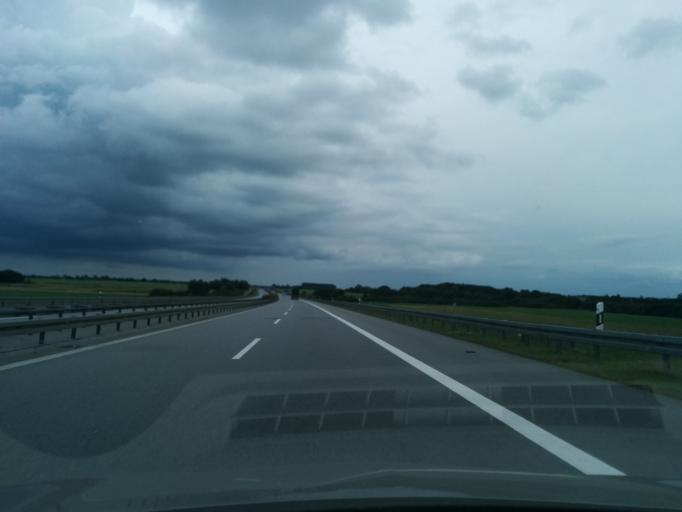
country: DE
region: Mecklenburg-Vorpommern
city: Brunn
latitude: 53.6759
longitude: 13.3359
